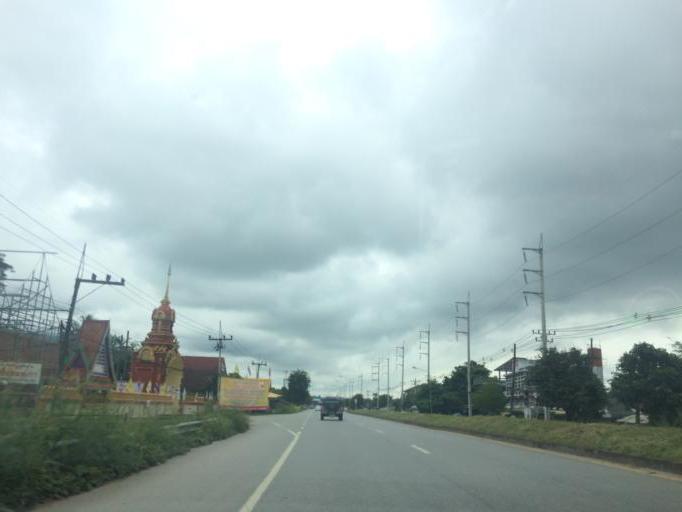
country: TH
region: Chiang Rai
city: Mae Chan
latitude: 20.0745
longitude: 99.8757
